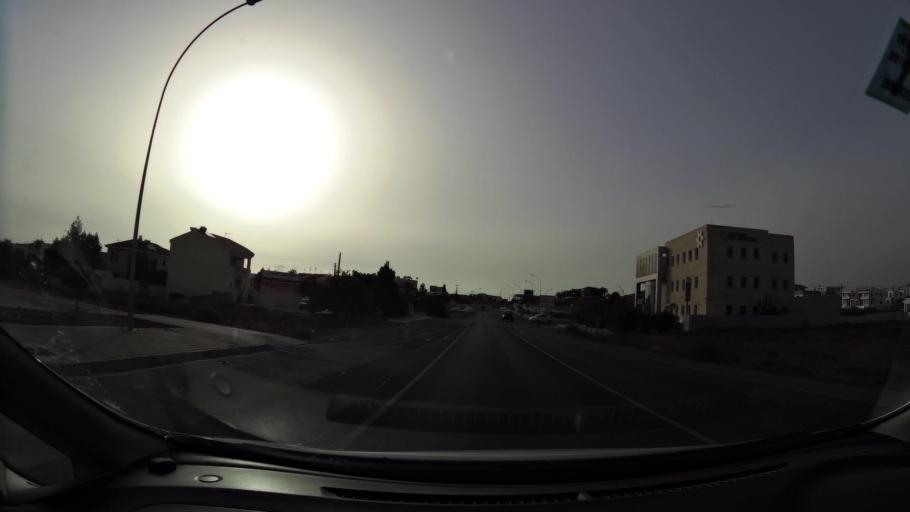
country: CY
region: Lefkosia
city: Geri
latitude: 35.0667
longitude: 33.3839
